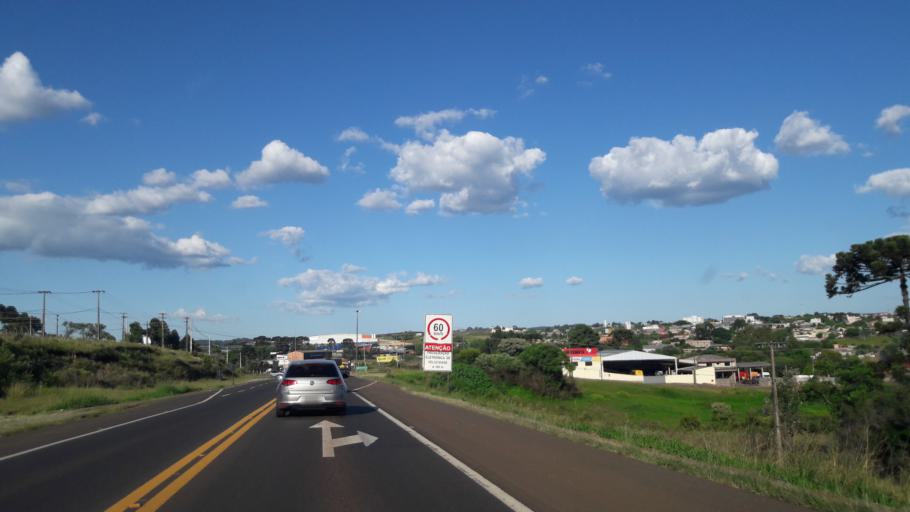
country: BR
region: Parana
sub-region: Guarapuava
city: Guarapuava
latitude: -25.3686
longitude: -51.4951
